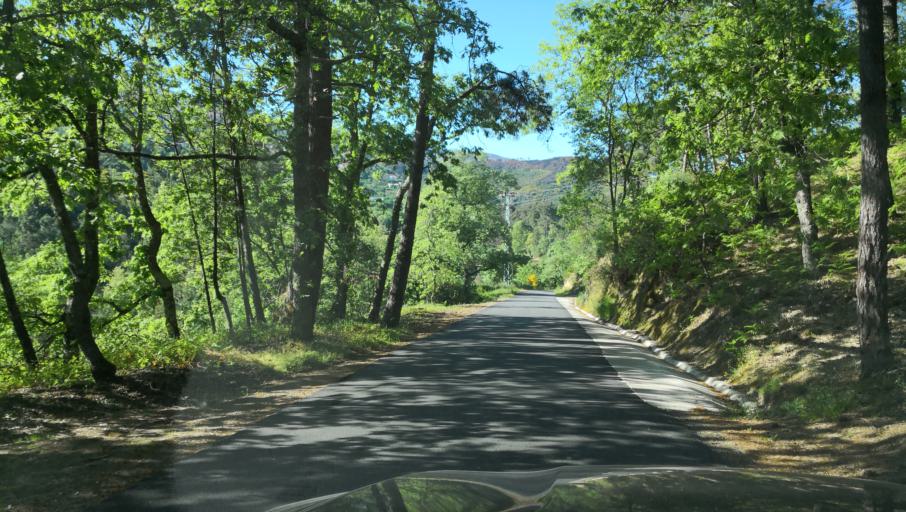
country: PT
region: Vila Real
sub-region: Vila Real
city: Vila Real
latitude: 41.3355
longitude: -7.7335
